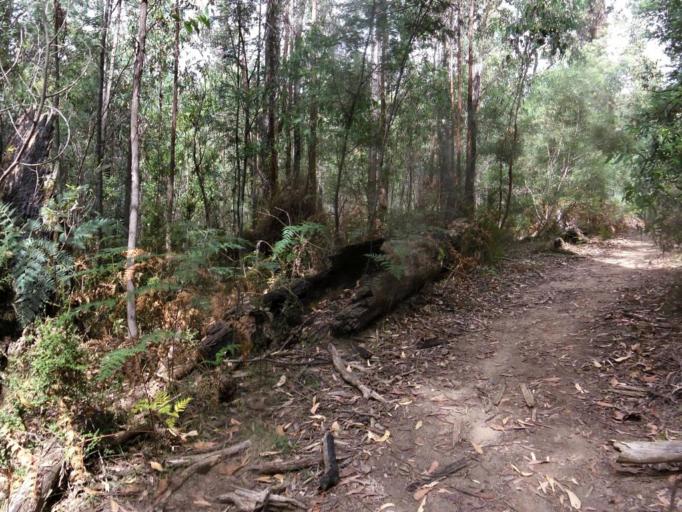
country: AU
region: Victoria
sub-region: Yarra Ranges
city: Healesville
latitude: -37.4031
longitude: 145.5657
